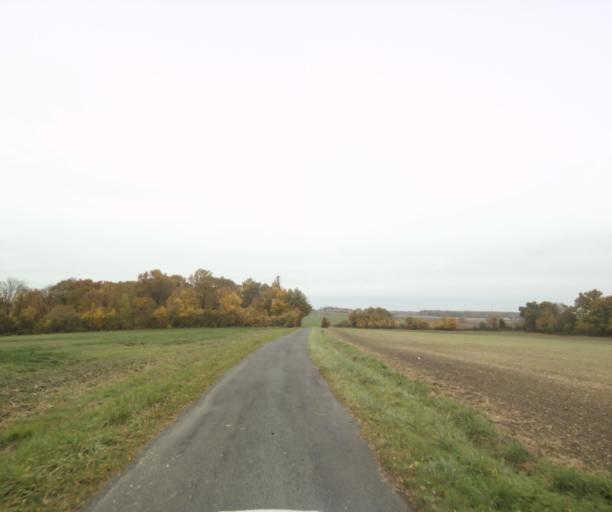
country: FR
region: Poitou-Charentes
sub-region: Departement de la Charente-Maritime
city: Chermignac
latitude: 45.7321
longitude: -0.6793
